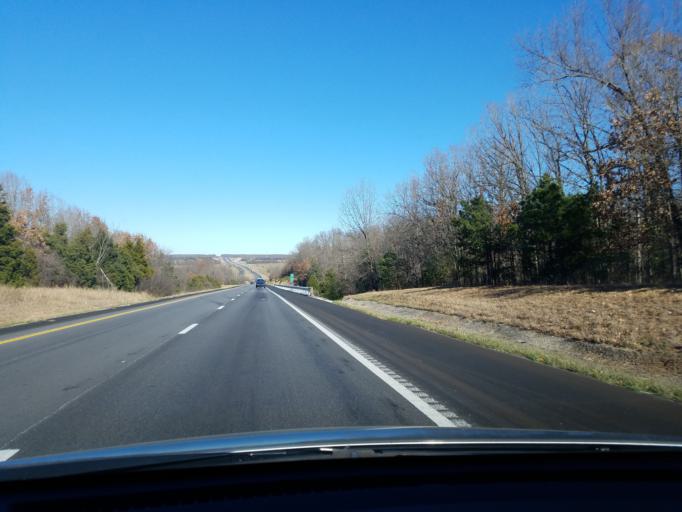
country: US
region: Missouri
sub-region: Webster County
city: Marshfield
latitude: 37.4028
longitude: -92.8942
